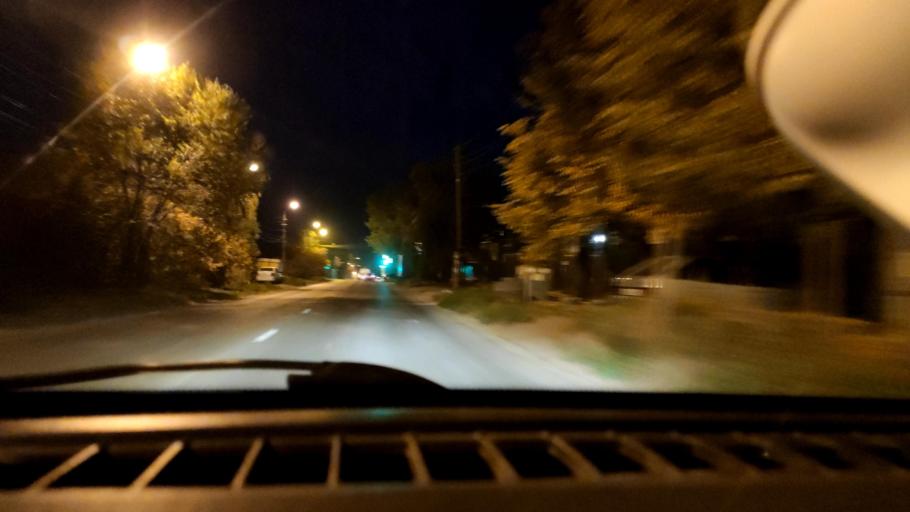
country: RU
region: Samara
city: Samara
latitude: 53.1774
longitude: 50.1694
